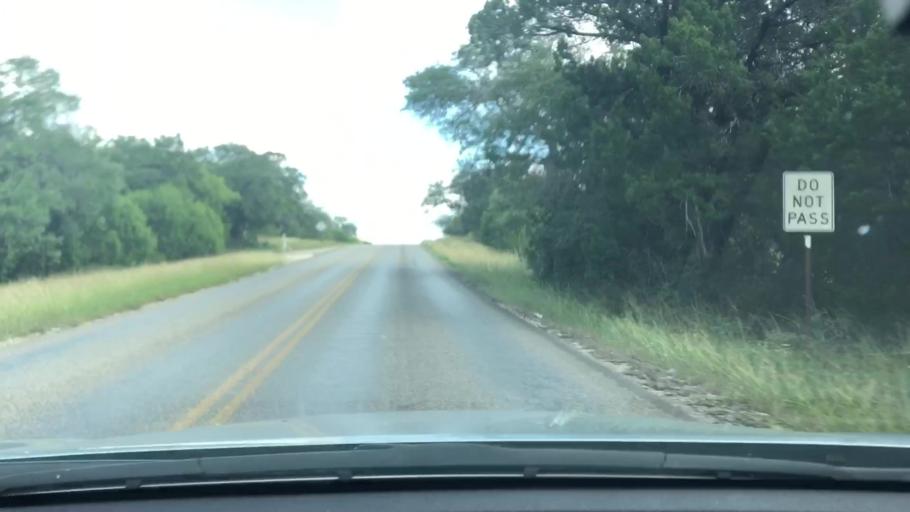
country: US
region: Texas
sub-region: Kendall County
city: Boerne
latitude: 29.7871
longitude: -98.6877
